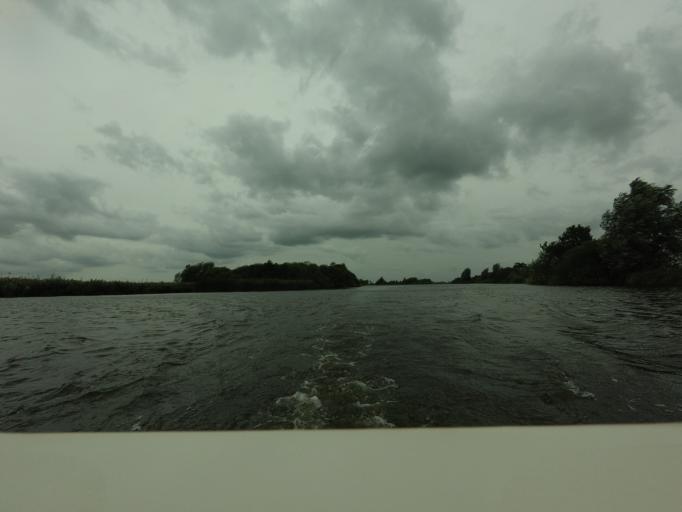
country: NL
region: Friesland
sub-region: Gemeente Boarnsterhim
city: Warten
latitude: 53.1007
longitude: 5.9135
